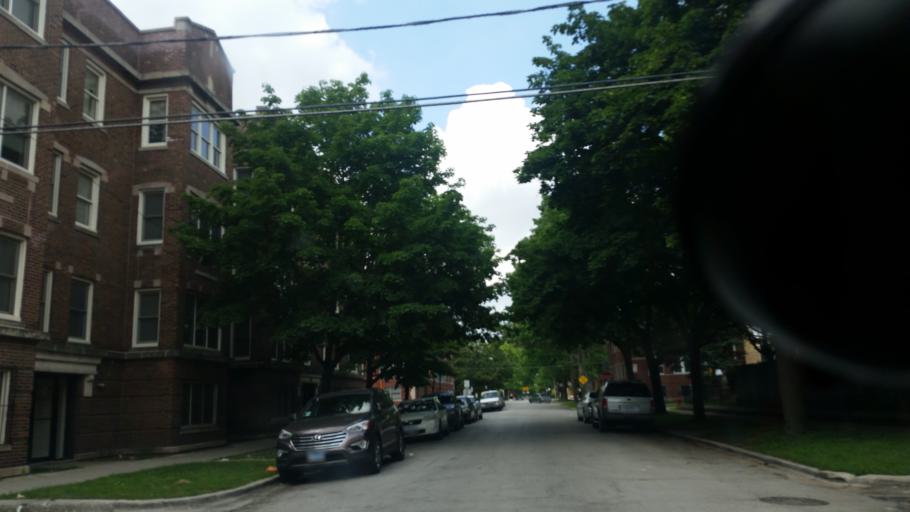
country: US
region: Illinois
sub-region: Cook County
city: Chicago
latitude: 41.7680
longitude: -87.5744
